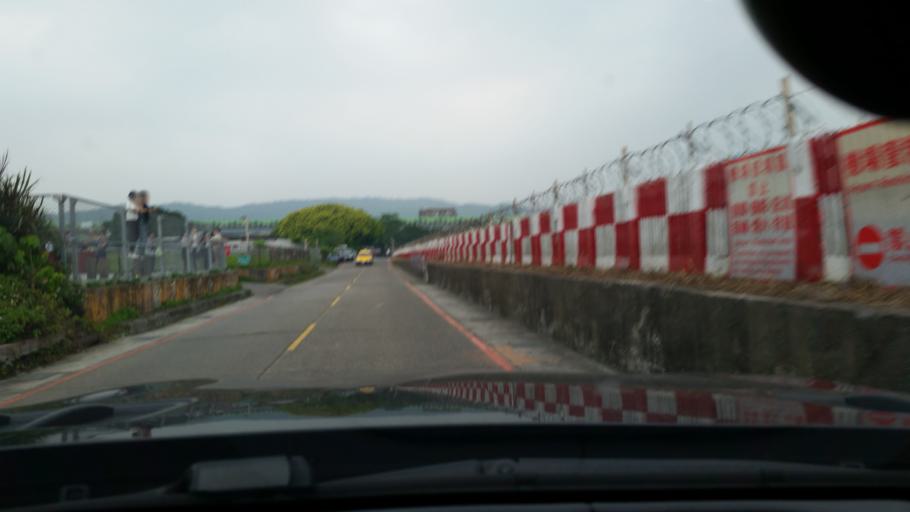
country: TW
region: Taipei
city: Taipei
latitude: 25.0699
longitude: 121.5385
